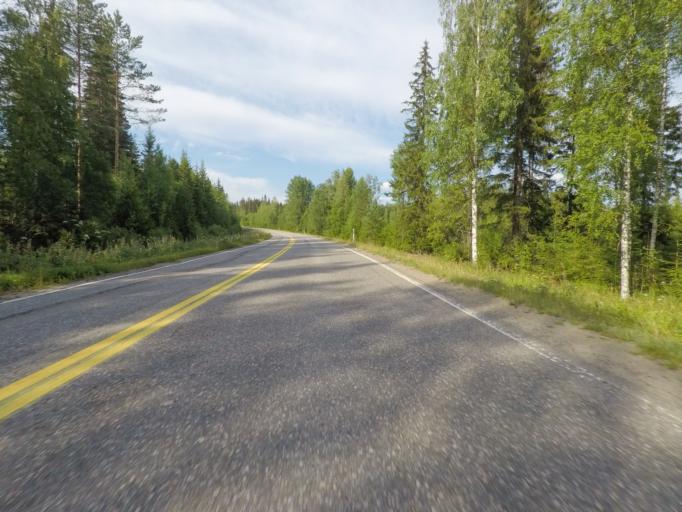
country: FI
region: Southern Savonia
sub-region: Savonlinna
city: Sulkava
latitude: 61.8447
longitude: 28.4710
